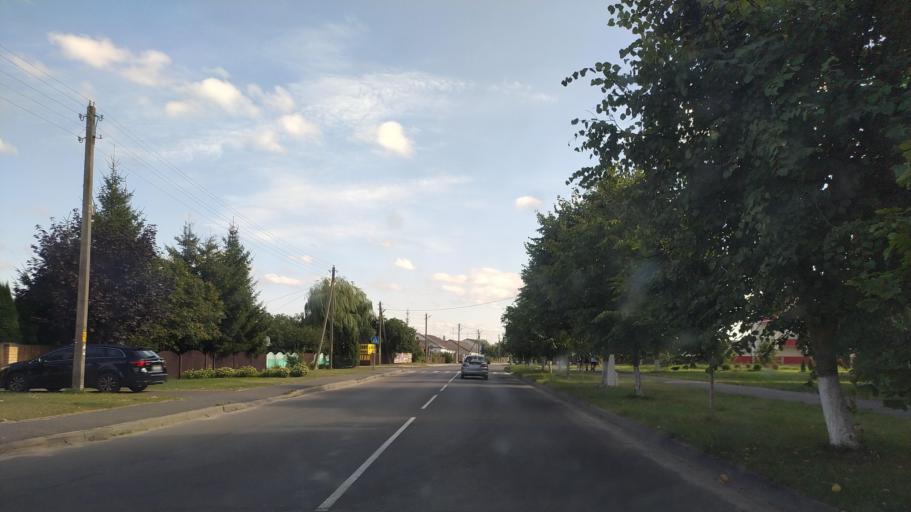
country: BY
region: Brest
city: Byaroza
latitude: 52.5290
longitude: 24.9876
